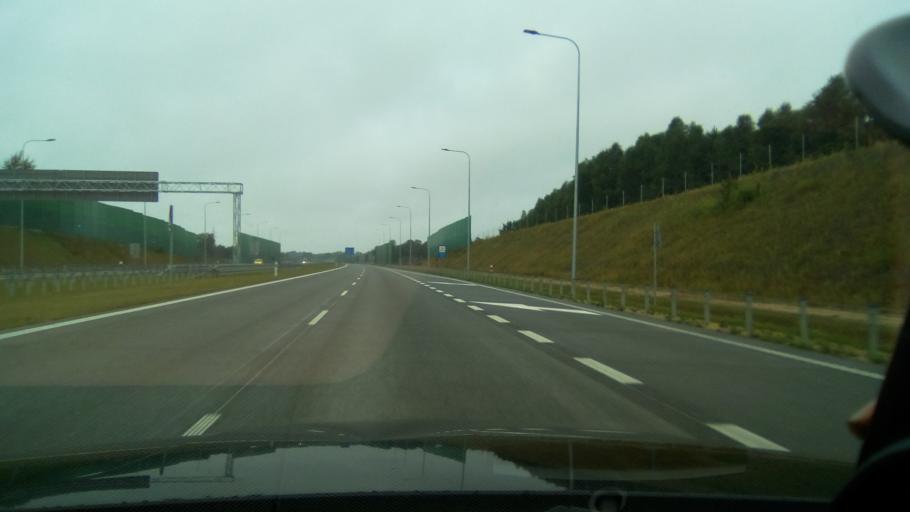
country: PL
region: Silesian Voivodeship
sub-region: Powiat klobucki
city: Kalej
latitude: 50.8442
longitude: 19.0372
